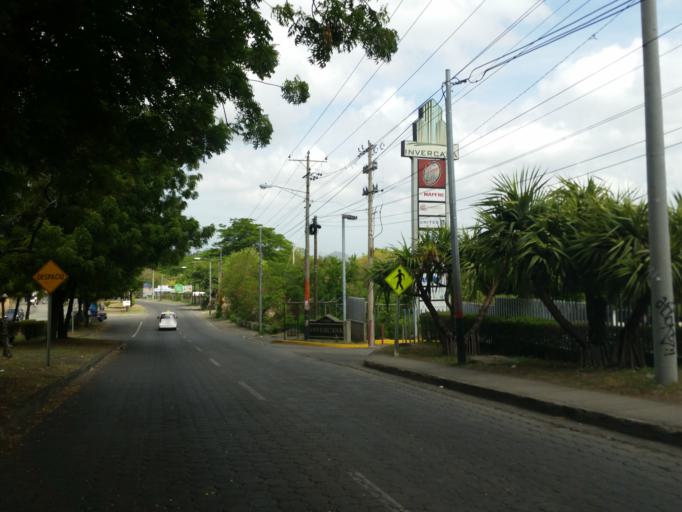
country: NI
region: Managua
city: Managua
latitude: 12.1127
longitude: -86.2662
